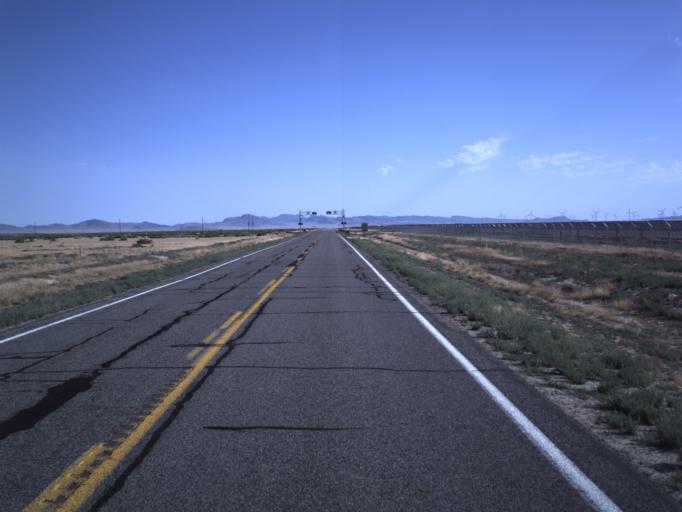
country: US
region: Utah
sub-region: Beaver County
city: Milford
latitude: 38.4918
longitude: -112.9911
